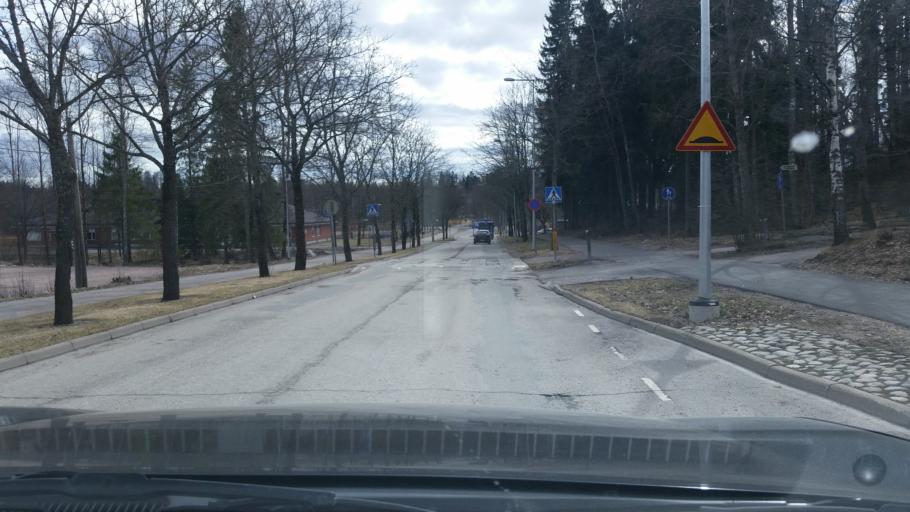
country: FI
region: Uusimaa
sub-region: Helsinki
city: Kilo
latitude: 60.2683
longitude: 24.8143
